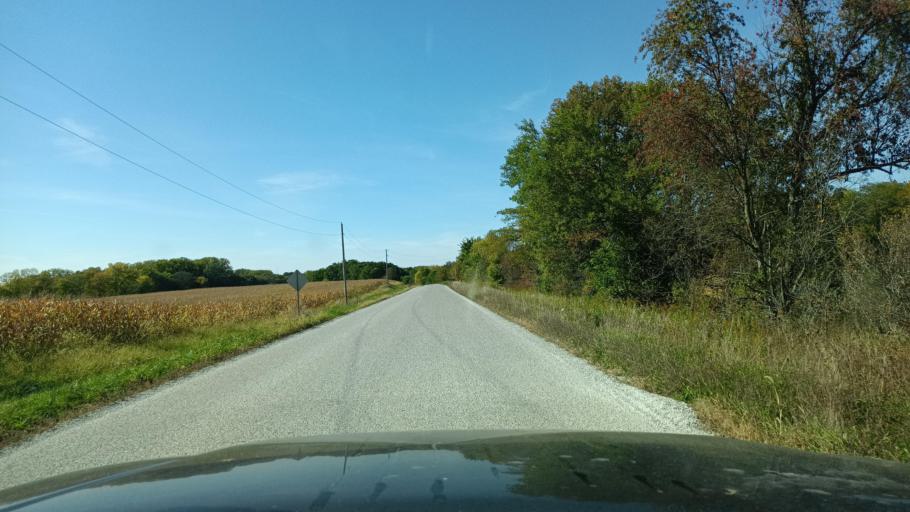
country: US
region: Illinois
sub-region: Logan County
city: Atlanta
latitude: 40.2349
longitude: -89.1586
